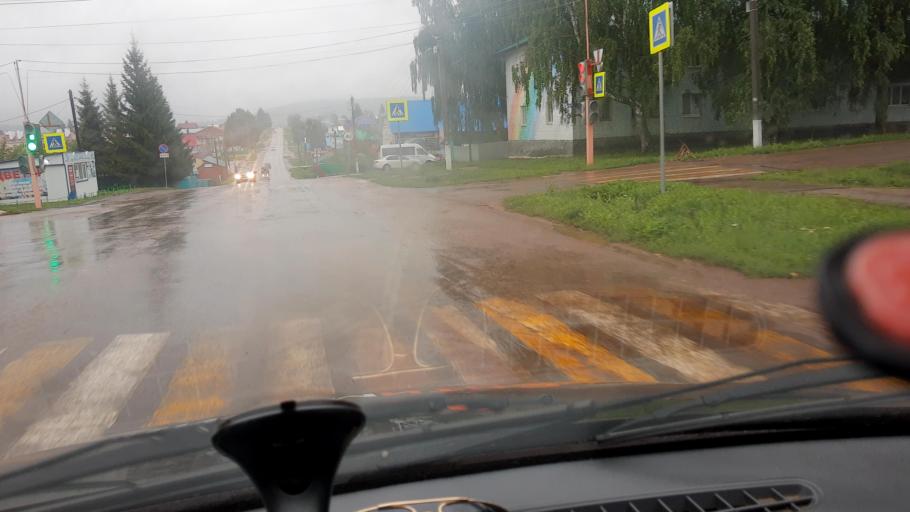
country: RU
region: Bashkortostan
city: Karmaskaly
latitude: 53.8914
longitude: 56.4648
